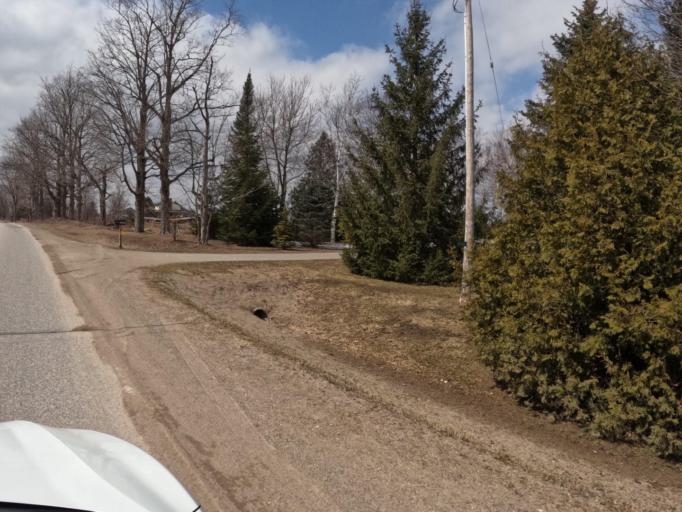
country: CA
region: Ontario
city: Shelburne
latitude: 44.0184
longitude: -80.1658
